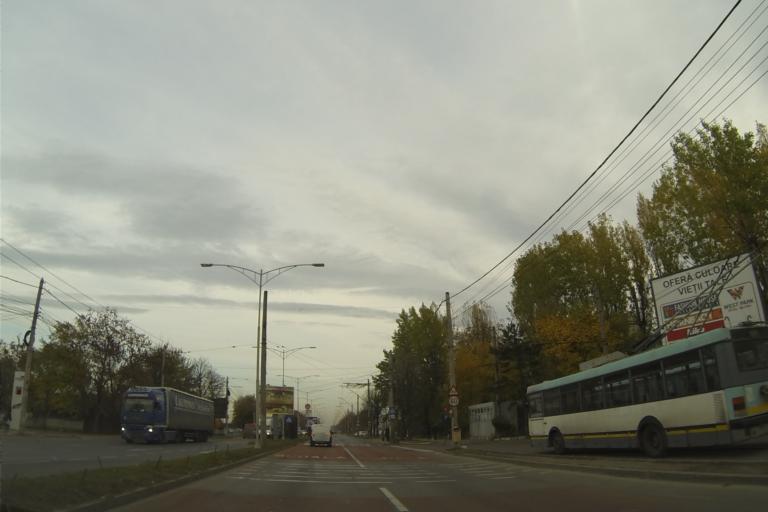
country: RO
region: Ilfov
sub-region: Comuna Chiajna
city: Chiajna
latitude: 44.4356
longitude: 25.9754
